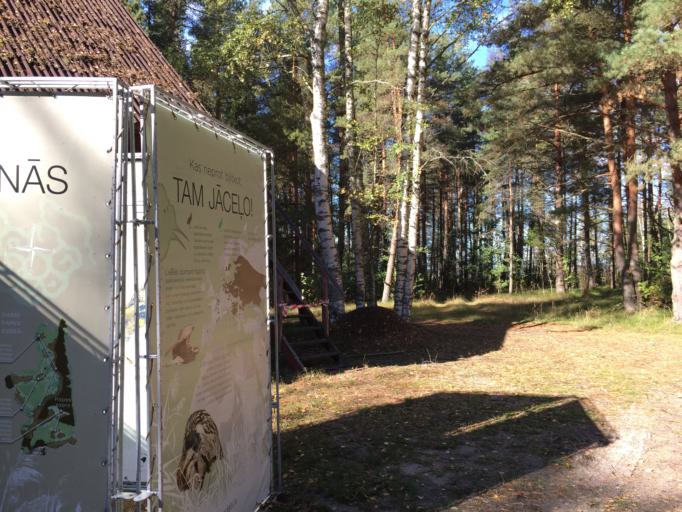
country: LV
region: Mesraga
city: Mersrags
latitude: 57.2606
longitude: 23.1351
